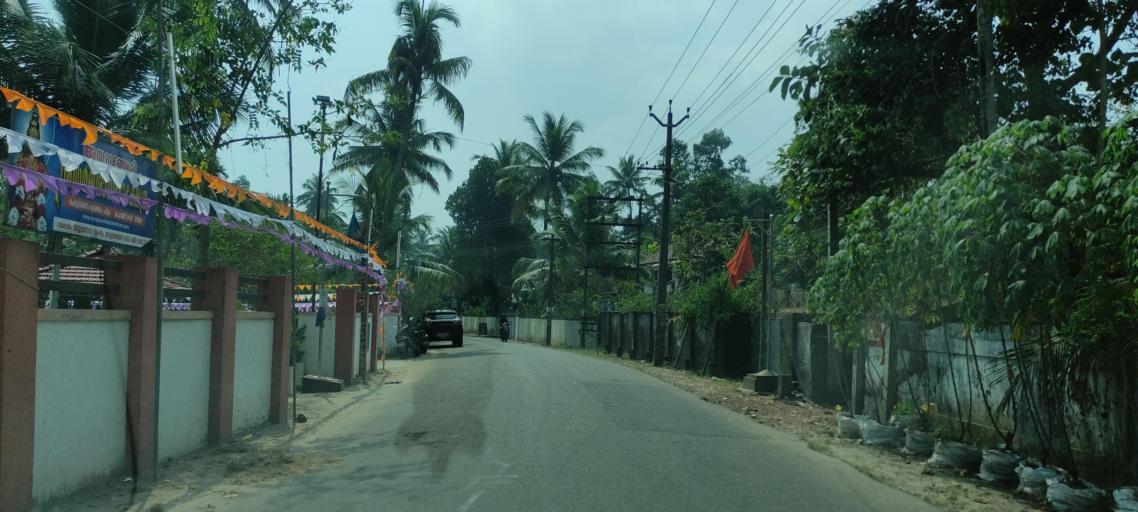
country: IN
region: Kerala
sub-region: Alappuzha
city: Shertallai
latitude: 9.6526
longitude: 76.3572
